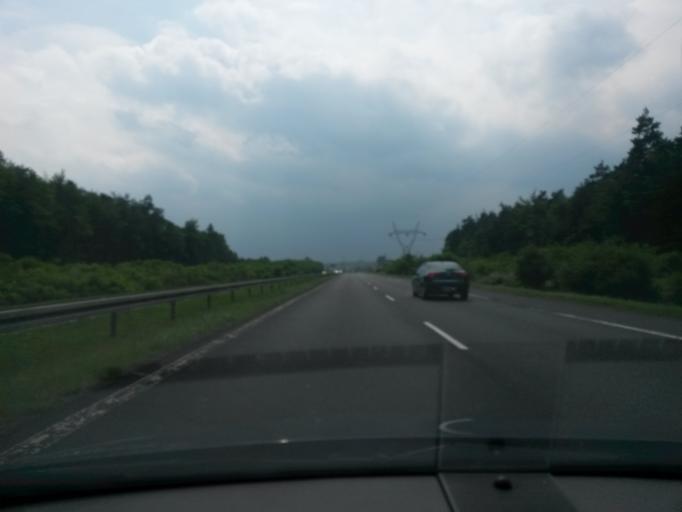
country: PL
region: Lodz Voivodeship
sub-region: Powiat radomszczanski
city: Radomsko
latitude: 51.1127
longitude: 19.3949
